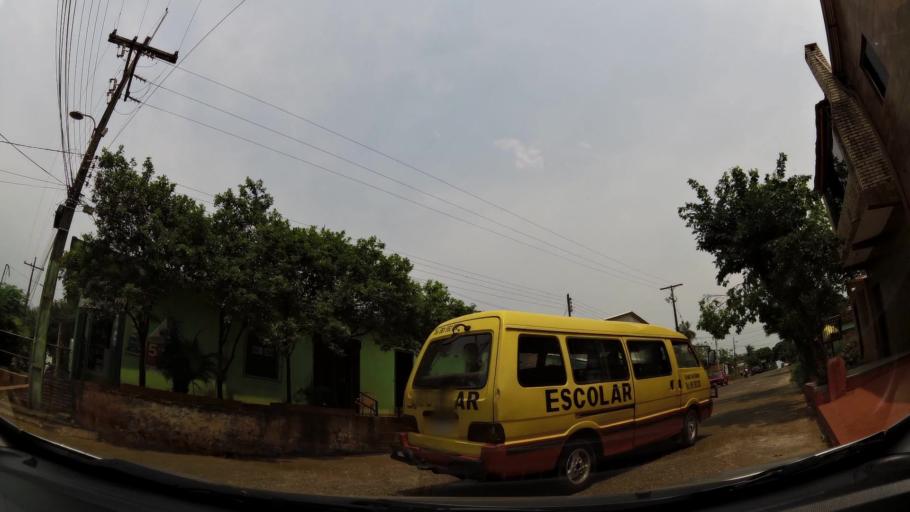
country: BR
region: Parana
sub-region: Foz Do Iguacu
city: Foz do Iguacu
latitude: -25.5656
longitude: -54.6106
